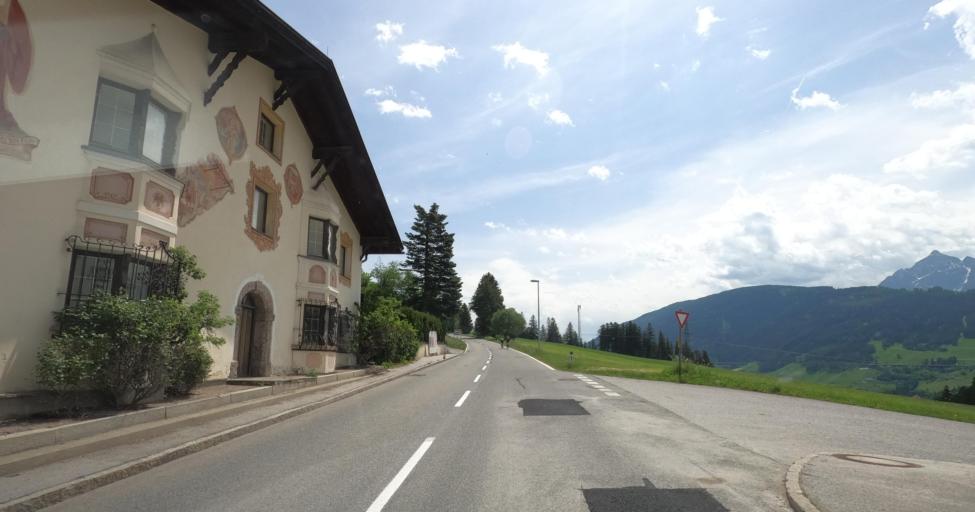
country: AT
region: Tyrol
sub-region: Politischer Bezirk Innsbruck Land
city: Patsch
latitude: 47.2018
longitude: 11.4185
